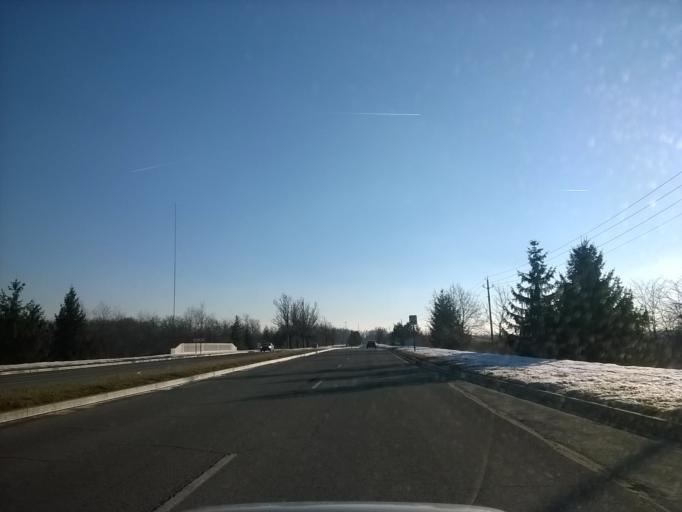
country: US
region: Indiana
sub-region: Hamilton County
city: Carmel
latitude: 39.9409
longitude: -86.0748
